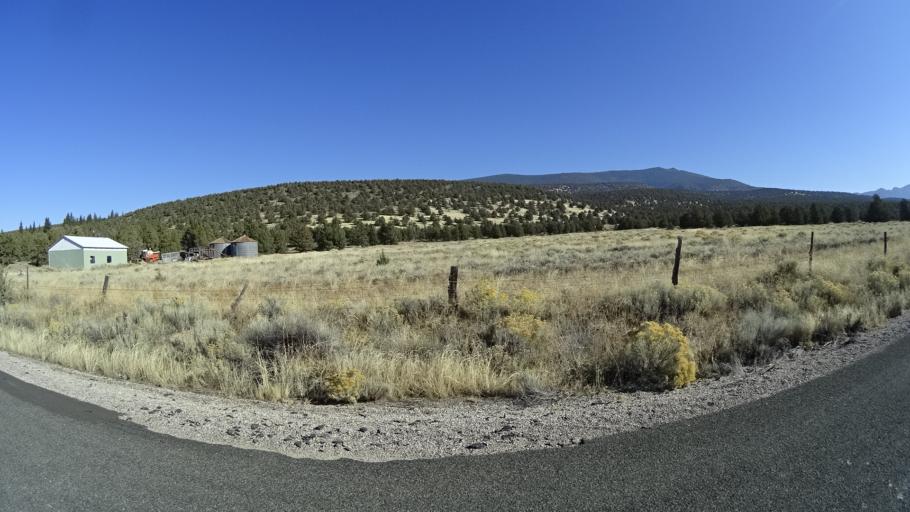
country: US
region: California
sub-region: Siskiyou County
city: Weed
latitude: 41.6182
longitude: -122.3209
